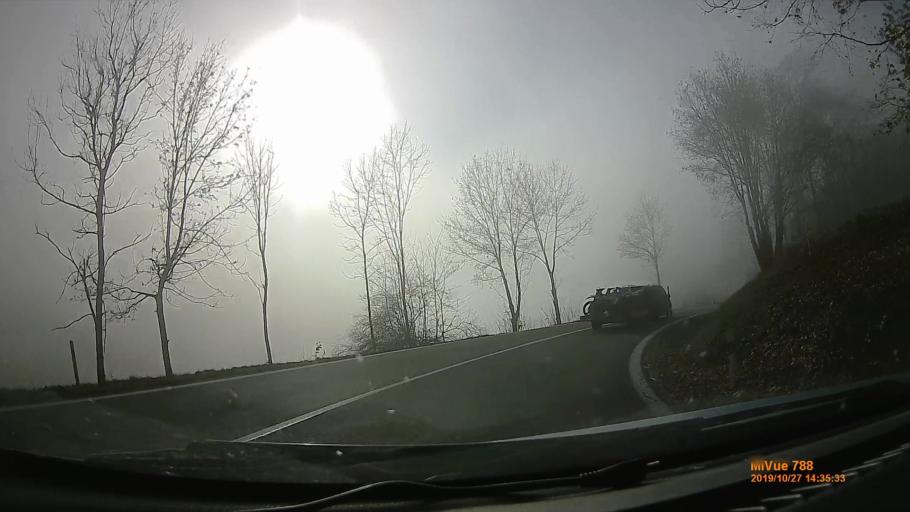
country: CZ
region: Olomoucky
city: Stity
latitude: 49.9899
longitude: 16.8026
